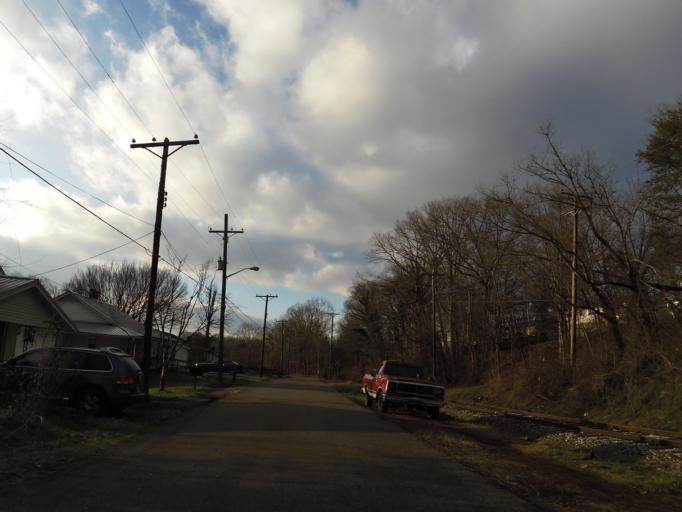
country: US
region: Tennessee
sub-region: Knox County
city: Knoxville
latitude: 35.9557
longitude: -83.8836
